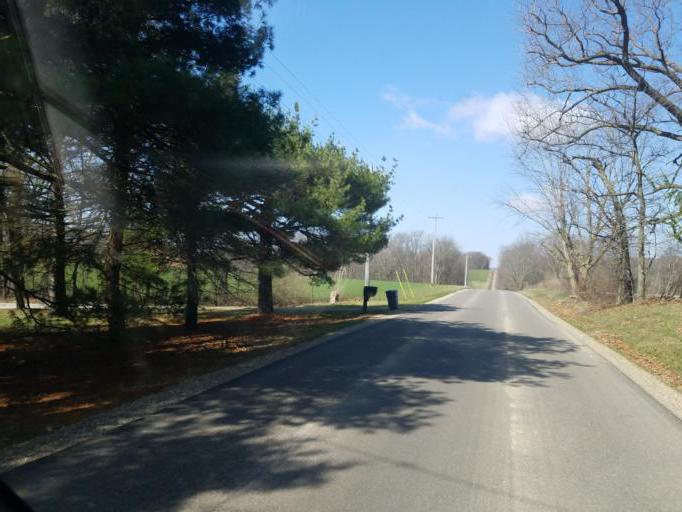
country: US
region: Ohio
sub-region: Licking County
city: Utica
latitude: 40.2475
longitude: -82.3411
